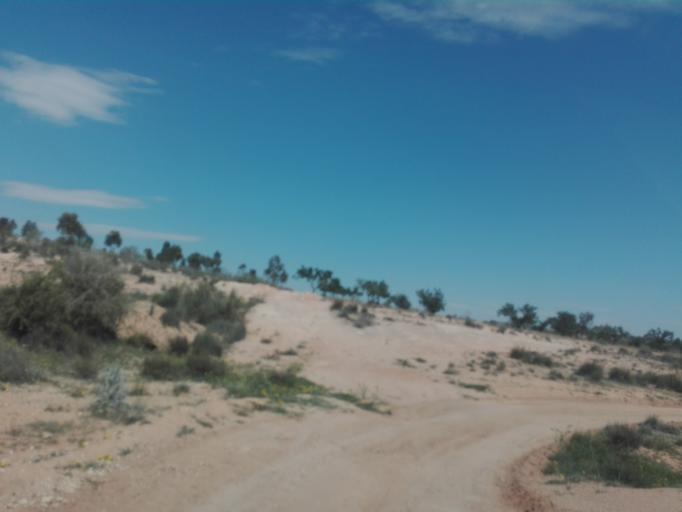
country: TN
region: Safaqis
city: Sfax
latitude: 34.6906
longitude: 10.5300
